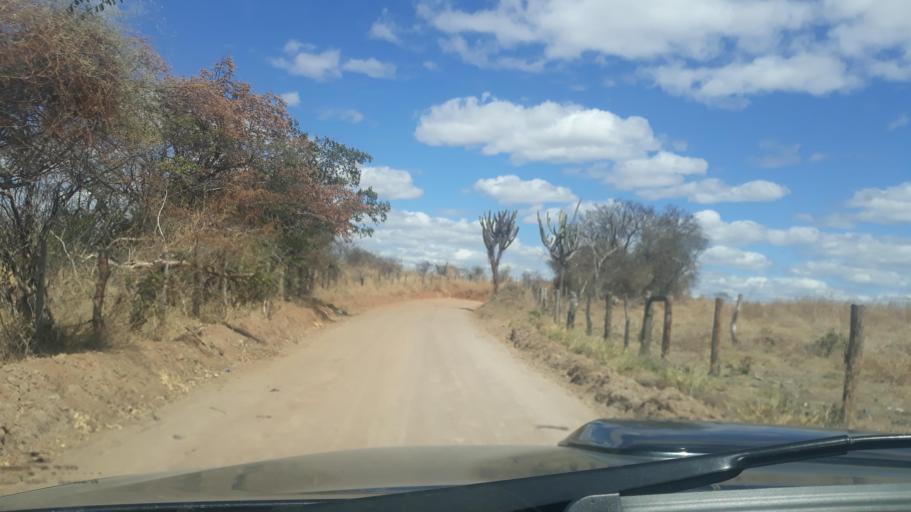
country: BR
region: Bahia
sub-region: Riacho De Santana
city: Riacho de Santana
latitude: -13.8967
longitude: -42.8499
